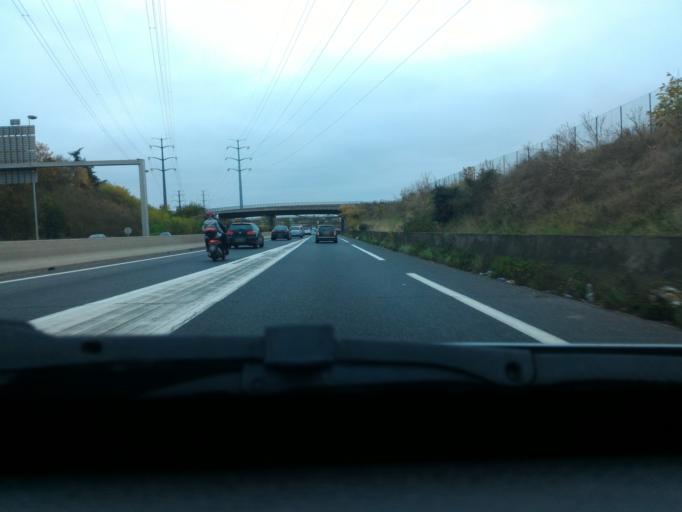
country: FR
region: Ile-de-France
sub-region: Departement du Val-de-Marne
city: Creteil
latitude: 48.7746
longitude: 2.4441
